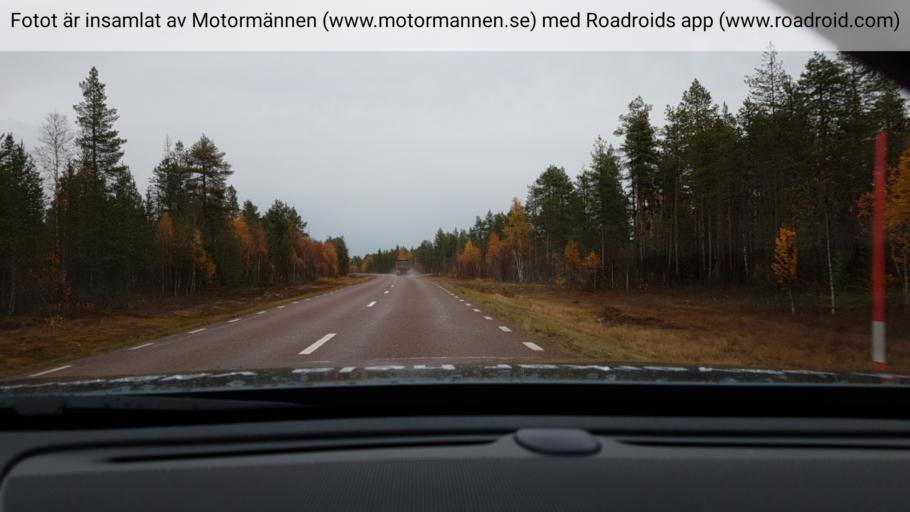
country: SE
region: Norrbotten
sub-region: Pajala Kommun
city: Pajala
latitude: 67.1741
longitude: 22.6887
